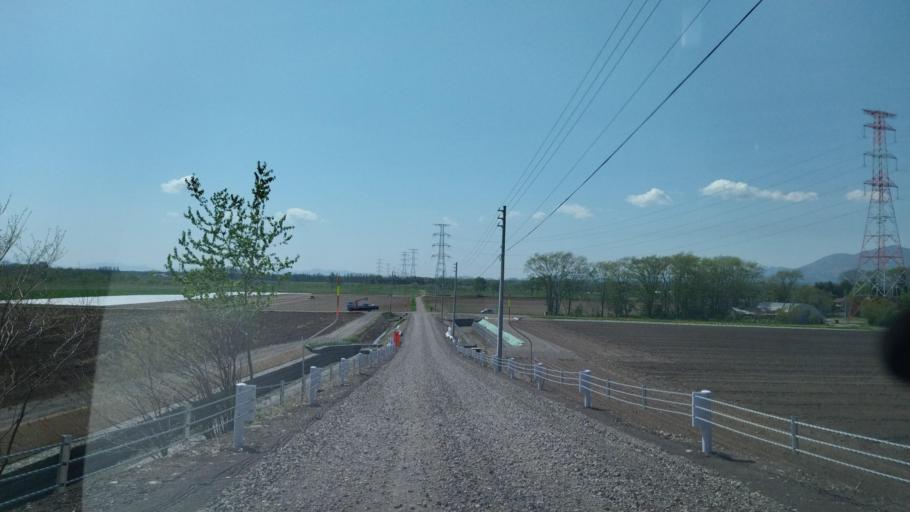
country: JP
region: Hokkaido
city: Otofuke
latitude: 43.1417
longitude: 143.2234
